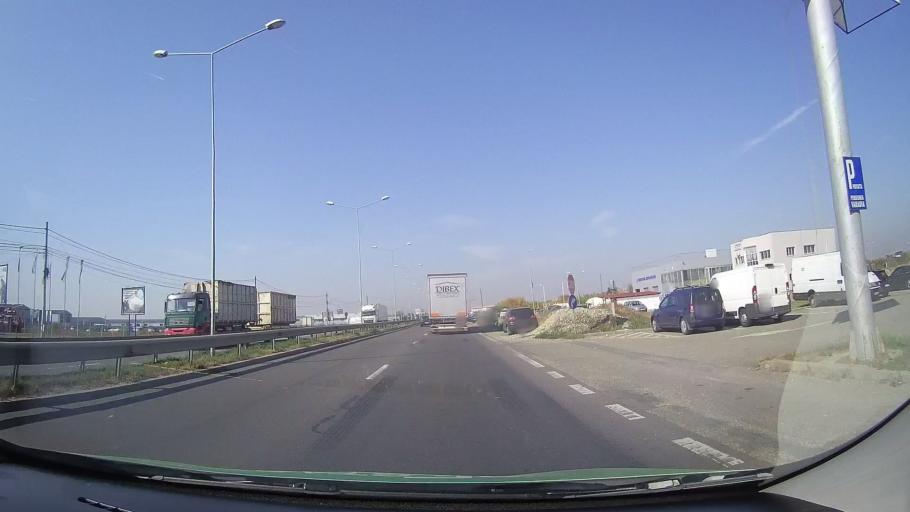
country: RO
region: Bihor
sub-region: Comuna Santandrei
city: Santandrei
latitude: 47.0481
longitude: 21.8933
